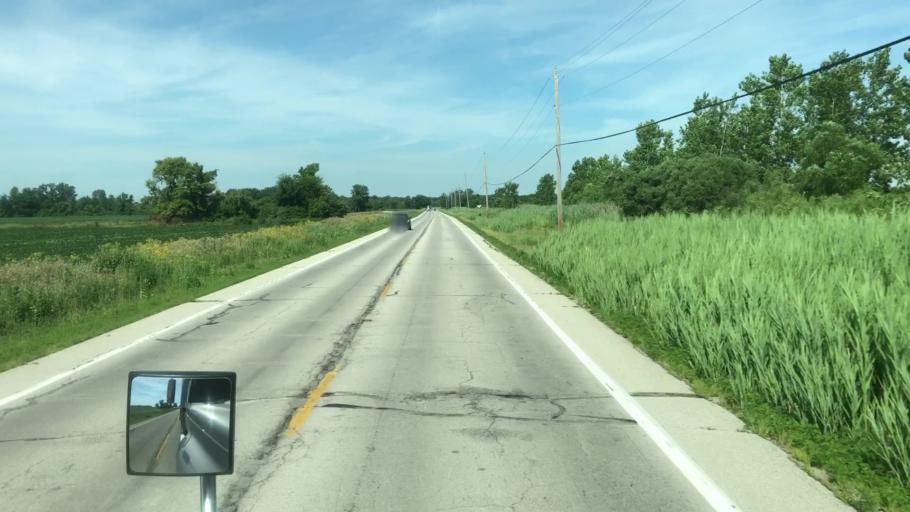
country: US
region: Ohio
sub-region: Ottawa County
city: Port Clinton
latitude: 41.4086
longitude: -82.9372
